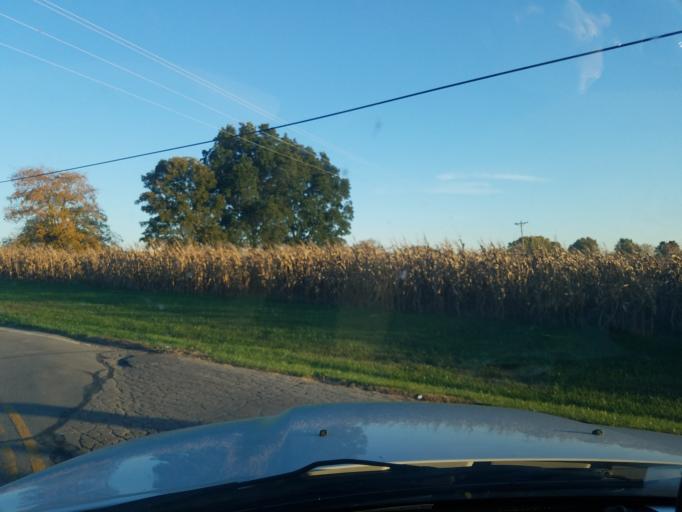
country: US
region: Indiana
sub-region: Floyd County
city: Galena
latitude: 38.4040
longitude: -85.9108
